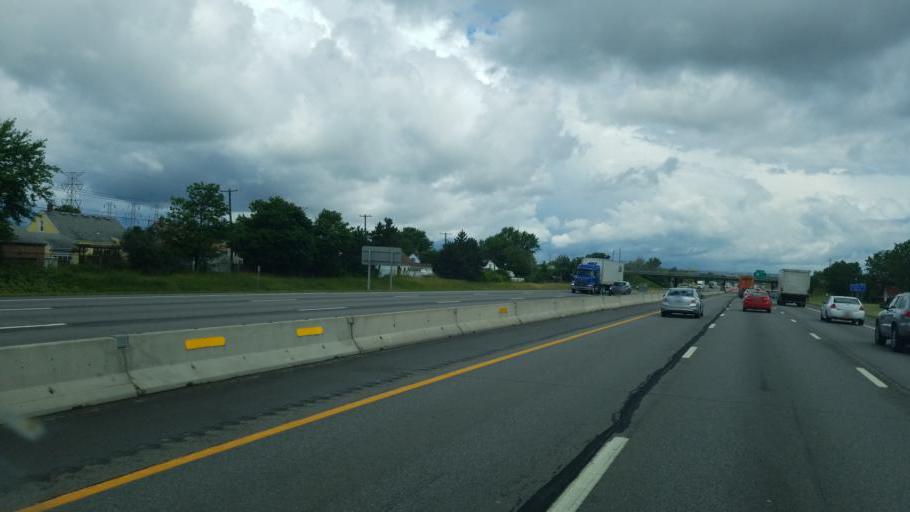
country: US
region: New York
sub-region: Erie County
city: Cheektowaga
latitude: 42.9221
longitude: -78.7661
